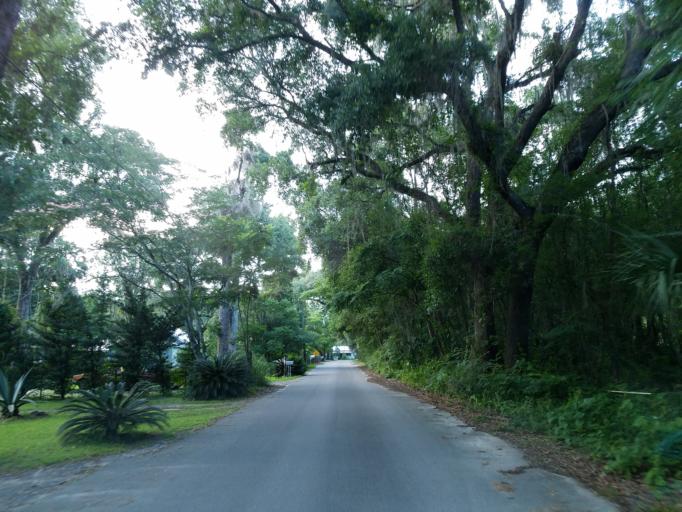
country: US
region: Florida
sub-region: Alachua County
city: Gainesville
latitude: 29.5011
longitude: -82.2827
